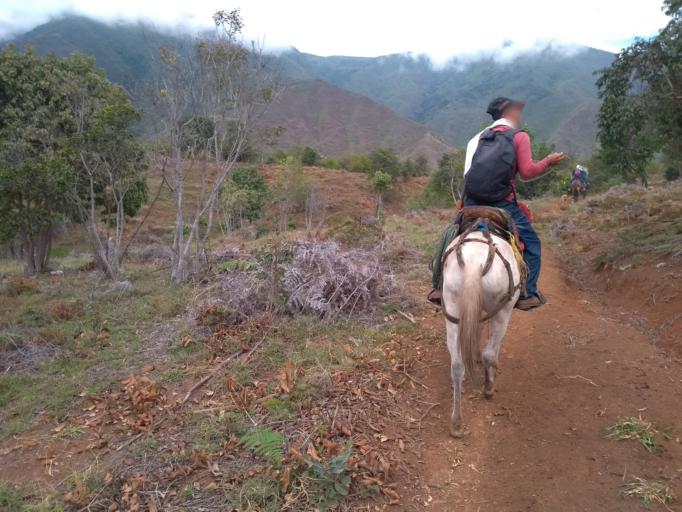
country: CO
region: Cesar
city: Manaure Balcon del Cesar
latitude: 10.1702
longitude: -73.0226
